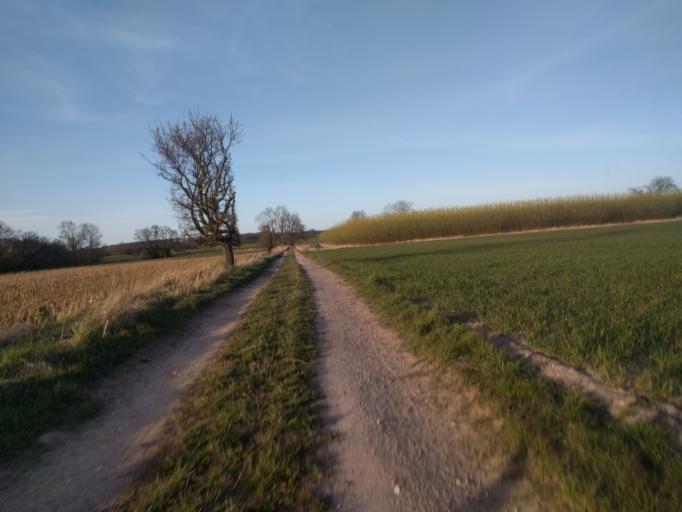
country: DK
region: South Denmark
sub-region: Kerteminde Kommune
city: Munkebo
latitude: 55.4122
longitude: 10.5446
